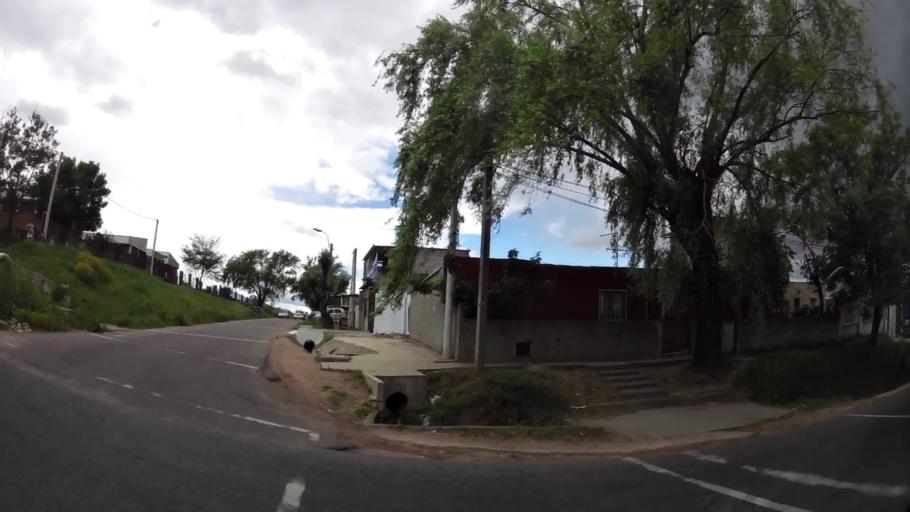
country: UY
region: Montevideo
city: Montevideo
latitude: -34.8331
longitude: -56.1681
